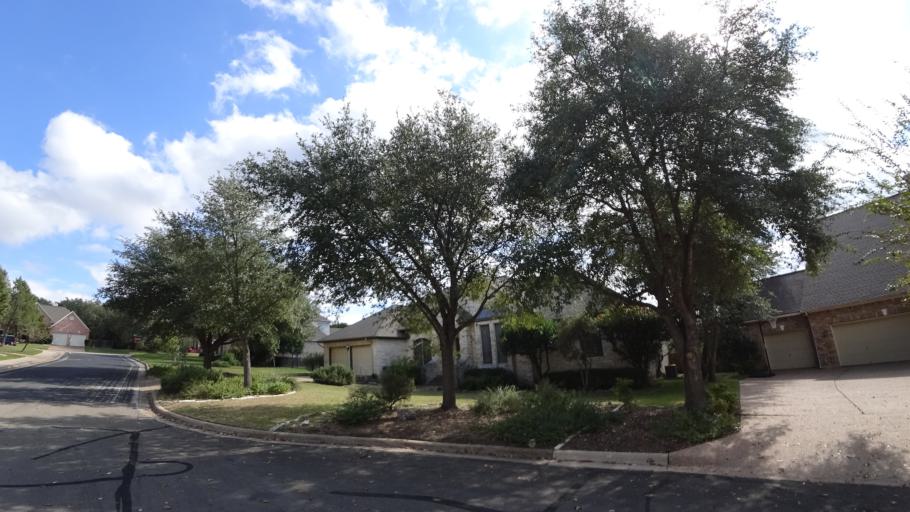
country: US
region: Texas
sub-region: Williamson County
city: Jollyville
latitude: 30.4173
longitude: -97.7923
